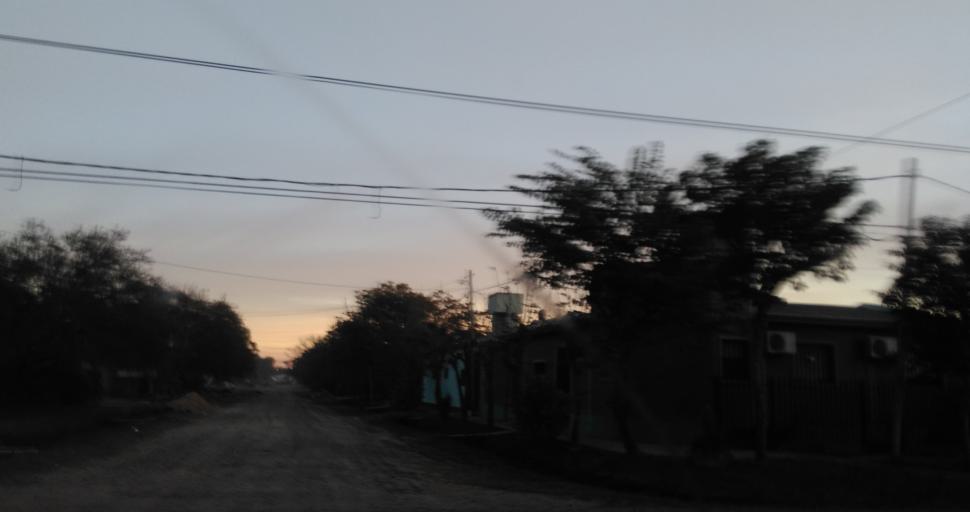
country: AR
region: Chaco
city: Resistencia
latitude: -27.4727
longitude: -58.9961
